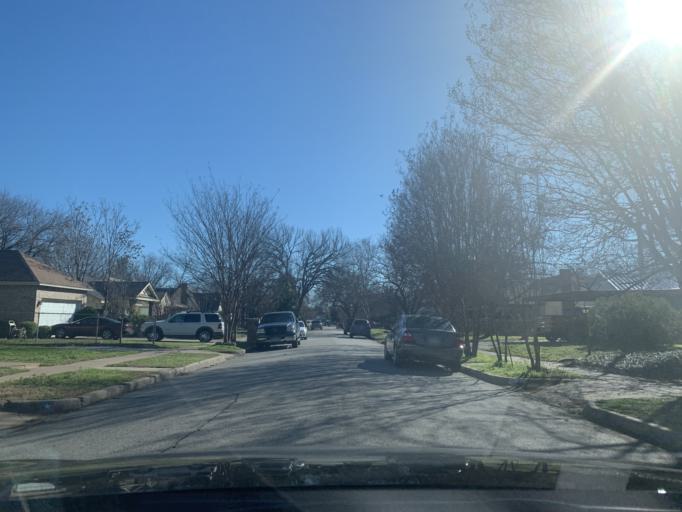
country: US
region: Texas
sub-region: Tarrant County
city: Haltom City
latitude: 32.7812
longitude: -97.2830
